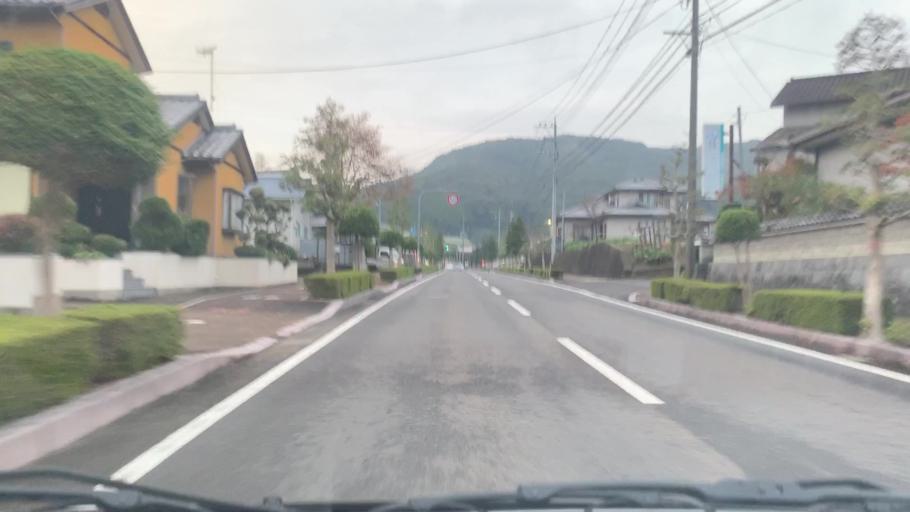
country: JP
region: Saga Prefecture
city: Ureshinomachi-shimojuku
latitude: 33.1480
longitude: 129.9003
